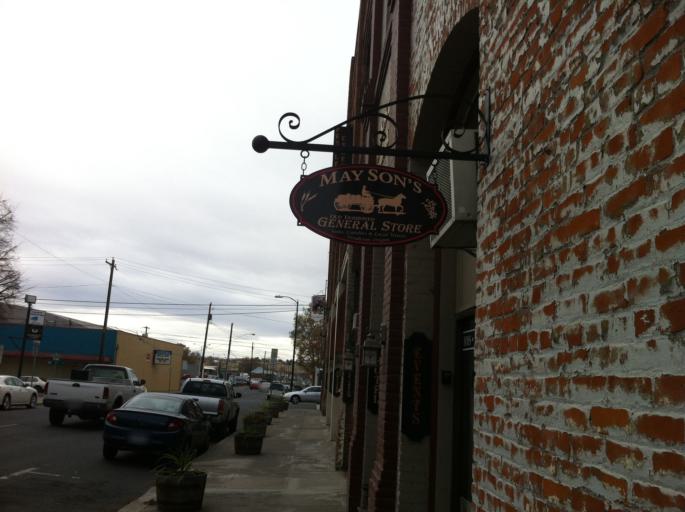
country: US
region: Oregon
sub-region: Umatilla County
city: Pendleton
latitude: 45.6706
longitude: -118.7866
